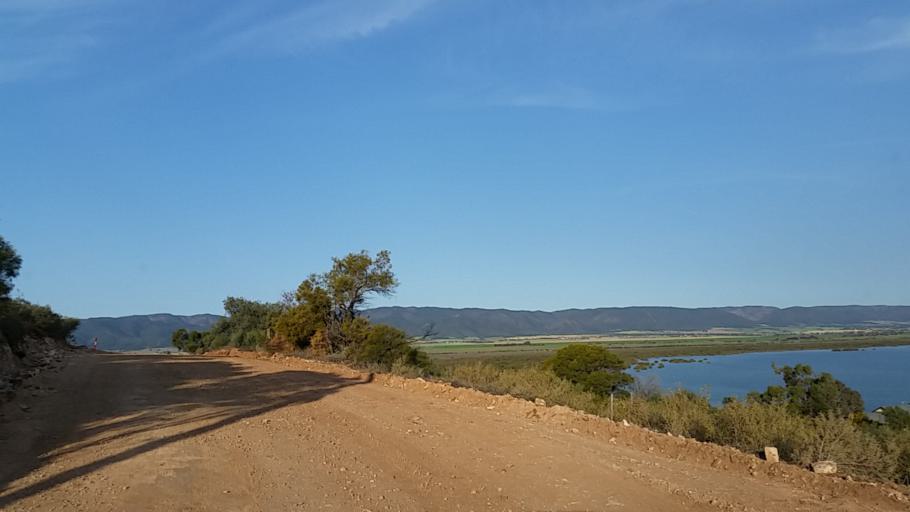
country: AU
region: South Australia
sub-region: Port Pirie City and Dists
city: Port Pirie
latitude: -33.1060
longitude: 138.0301
